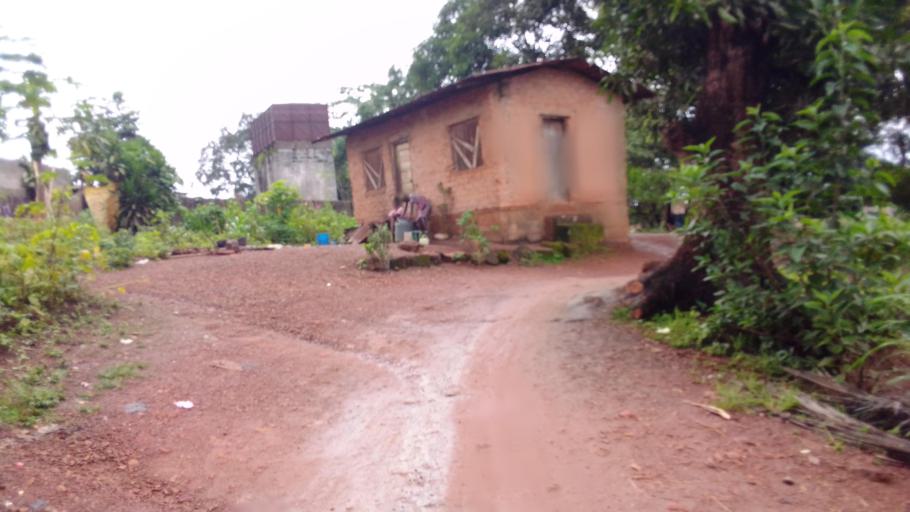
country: SL
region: Eastern Province
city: Kenema
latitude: 7.8729
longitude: -11.1803
